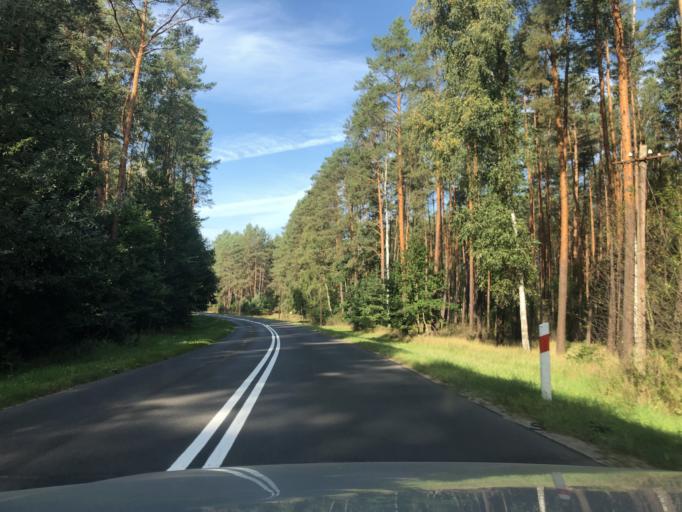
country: PL
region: Greater Poland Voivodeship
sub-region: Powiat pilski
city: Kaczory
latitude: 53.1112
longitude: 16.8598
